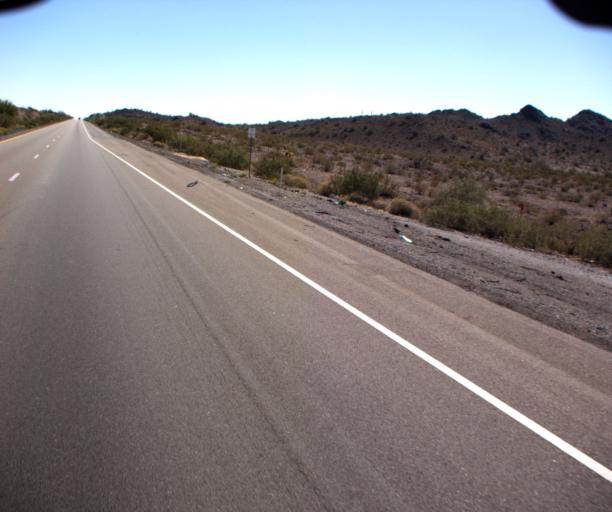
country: US
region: Arizona
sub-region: La Paz County
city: Salome
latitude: 33.6116
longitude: -113.6389
